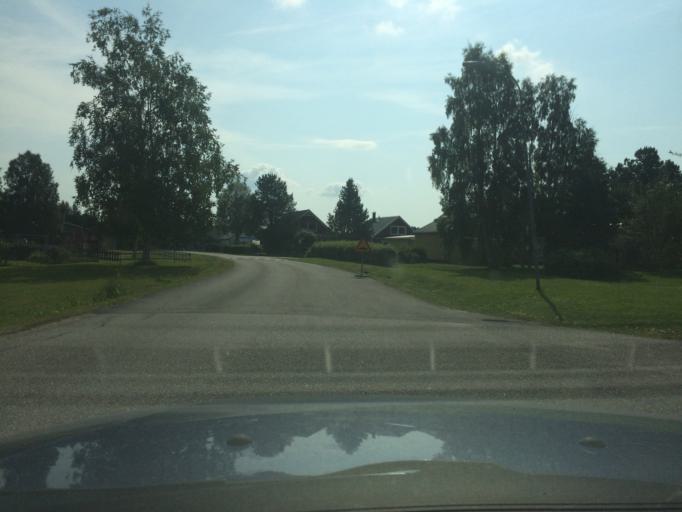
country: SE
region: Norrbotten
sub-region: Pitea Kommun
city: Bergsviken
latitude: 65.3477
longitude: 21.4165
